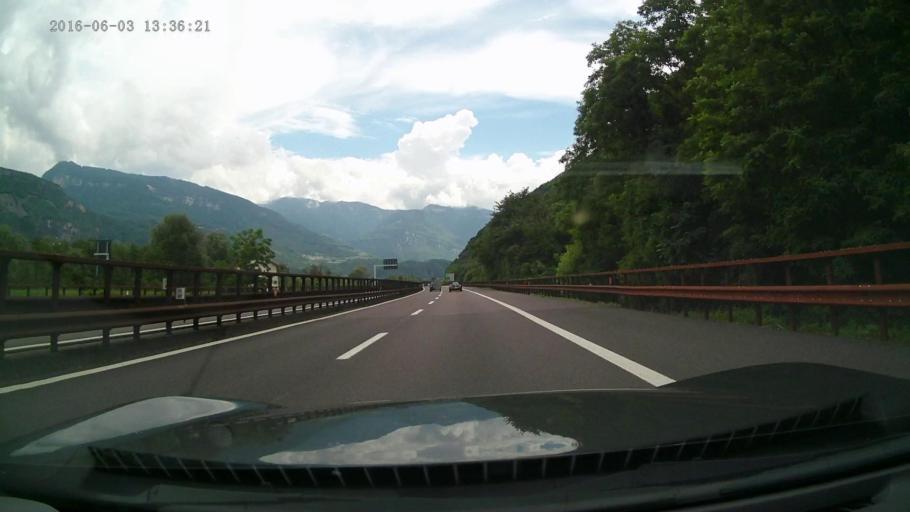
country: IT
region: Trentino-Alto Adige
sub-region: Bolzano
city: Ora
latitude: 46.3733
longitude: 11.2904
